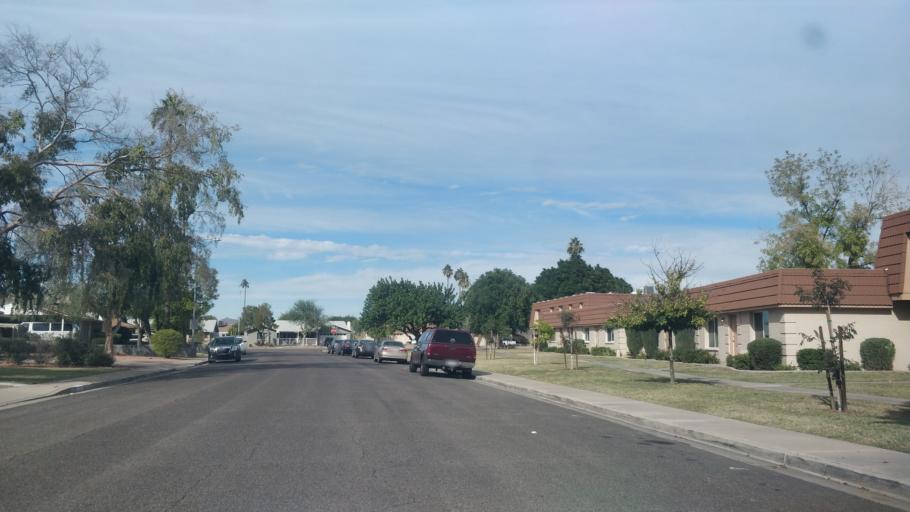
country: US
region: Arizona
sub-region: Maricopa County
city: Tempe
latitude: 33.3802
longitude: -111.9138
